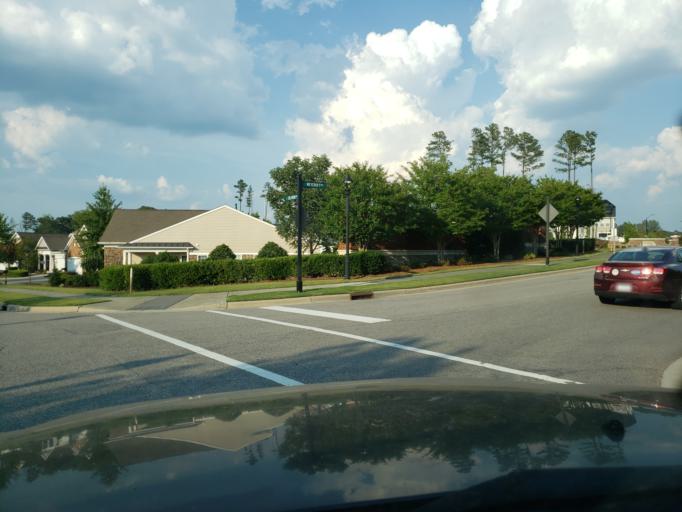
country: US
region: North Carolina
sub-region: Wake County
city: Green Level
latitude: 35.8362
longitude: -78.9128
